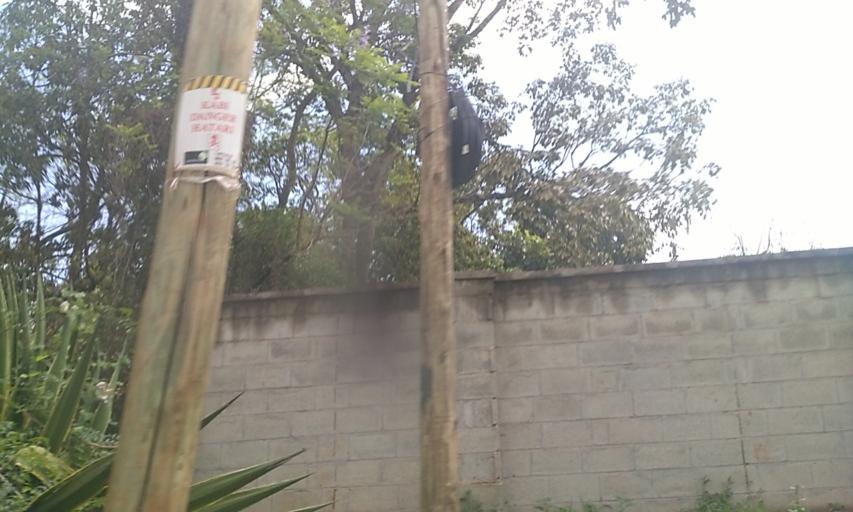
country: UG
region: Central Region
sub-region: Kampala District
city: Kampala
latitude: 0.3342
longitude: 32.5986
